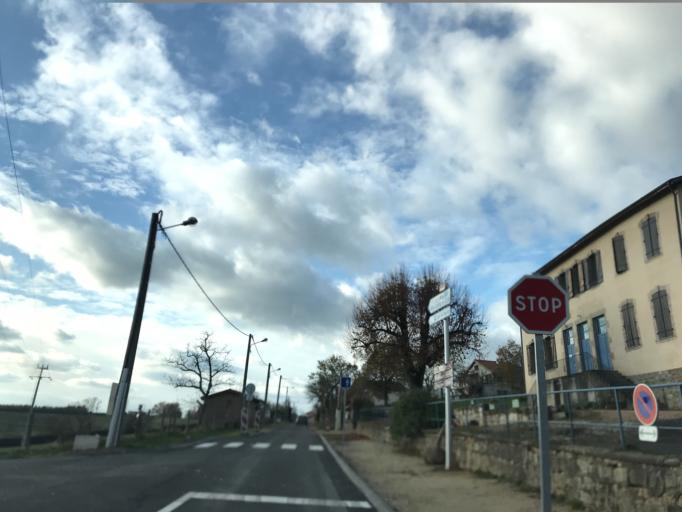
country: FR
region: Auvergne
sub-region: Departement du Puy-de-Dome
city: Courpiere
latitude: 45.7557
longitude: 3.6151
